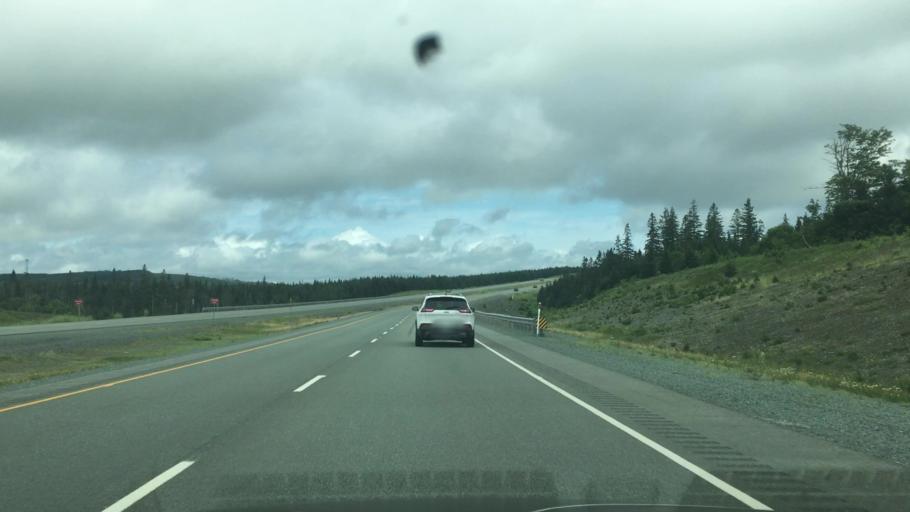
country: CA
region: Nova Scotia
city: Oxford
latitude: 45.5491
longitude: -63.7128
